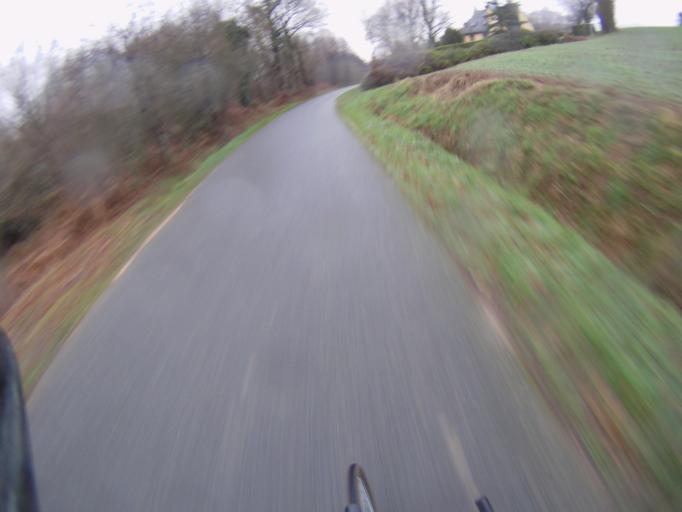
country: FR
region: Brittany
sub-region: Departement d'Ille-et-Vilaine
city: Chanteloup
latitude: 47.9359
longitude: -1.6037
